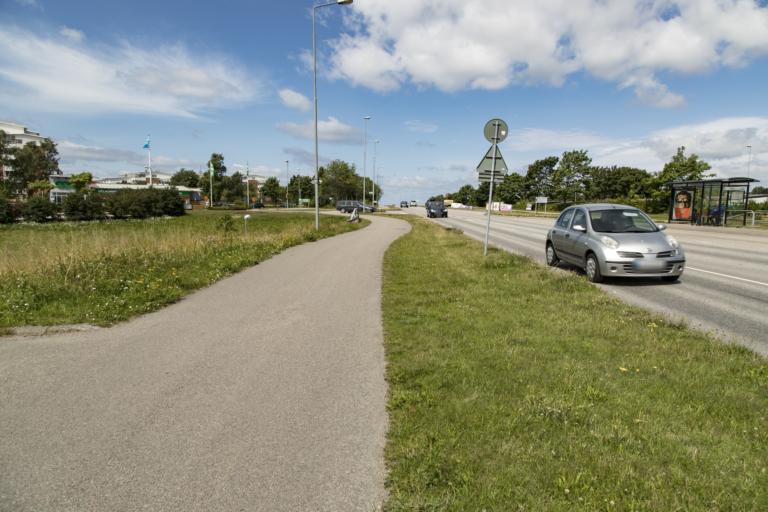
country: SE
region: Halland
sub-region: Varbergs Kommun
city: Varberg
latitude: 57.0920
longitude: 12.2613
